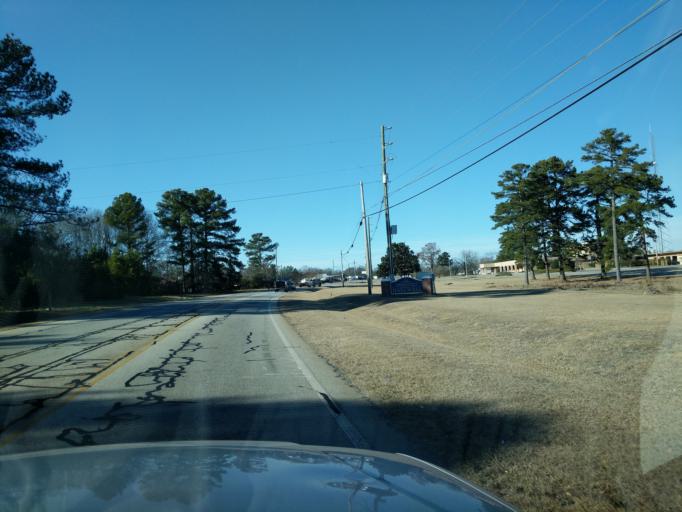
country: US
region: Georgia
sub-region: Hart County
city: Hartwell
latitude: 34.3360
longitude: -82.9199
